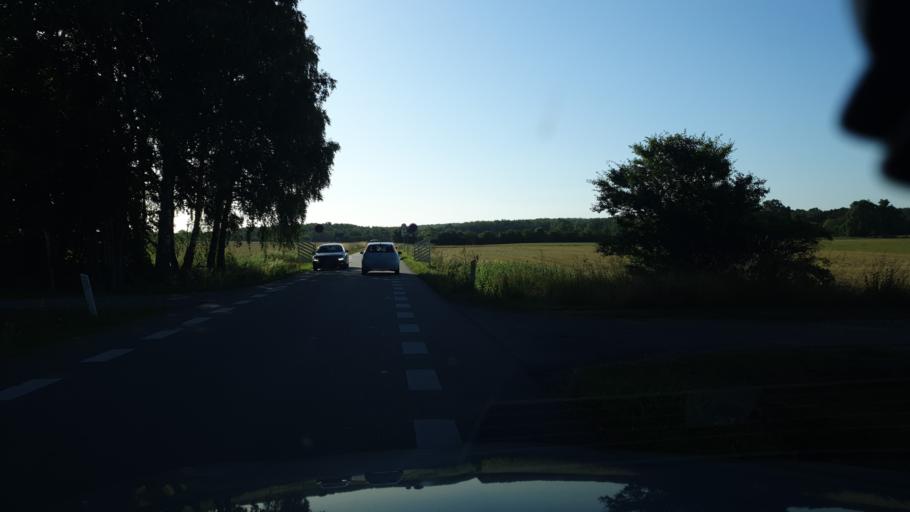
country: DK
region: Zealand
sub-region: Soro Kommune
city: Frederiksberg
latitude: 55.4088
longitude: 11.6111
